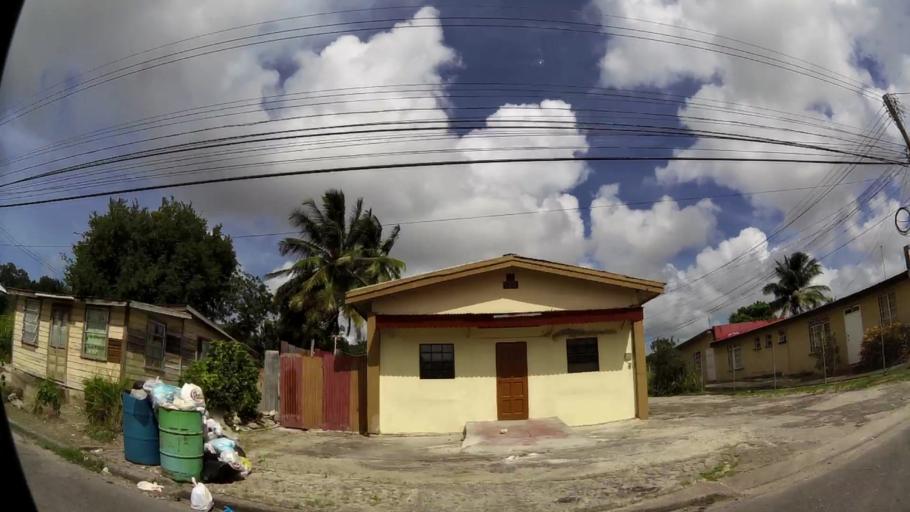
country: BB
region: Saint Michael
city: Bridgetown
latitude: 13.1225
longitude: -59.6144
